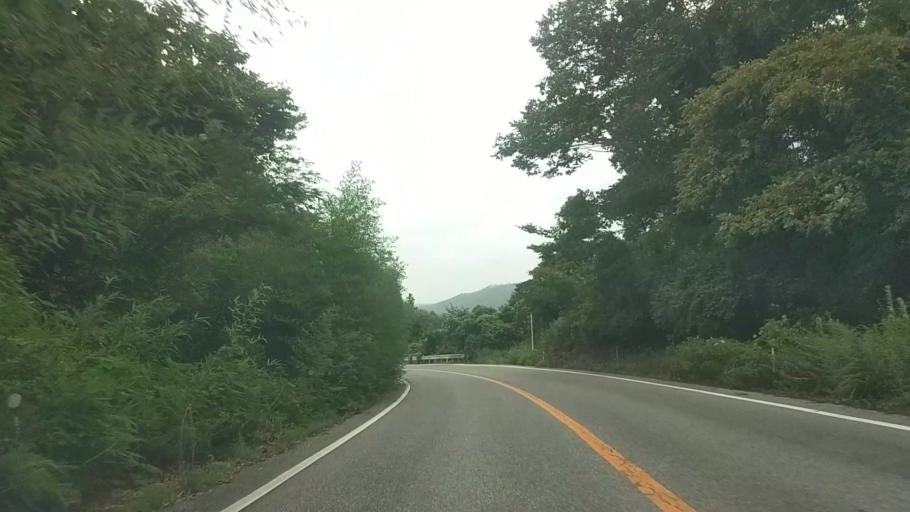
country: JP
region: Chiba
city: Kimitsu
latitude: 35.2423
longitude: 140.0065
